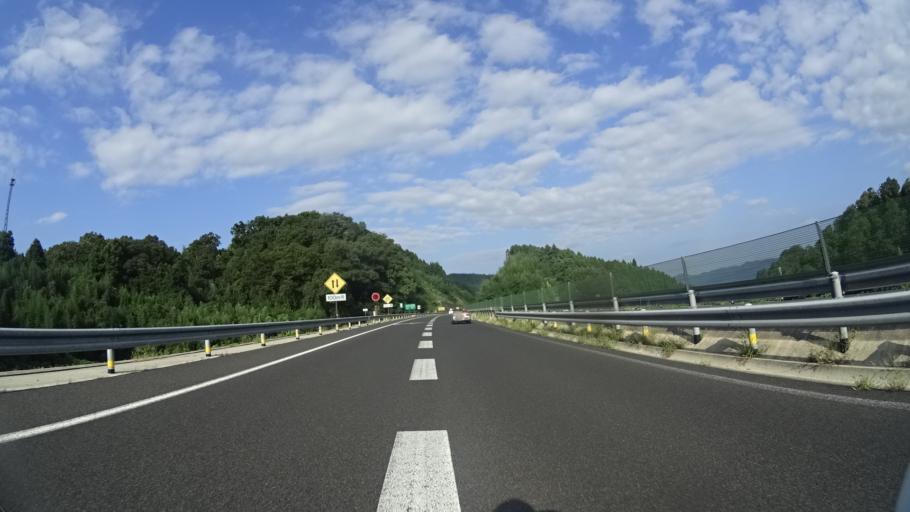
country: JP
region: Shimane
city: Izumo
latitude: 35.3382
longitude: 132.8056
